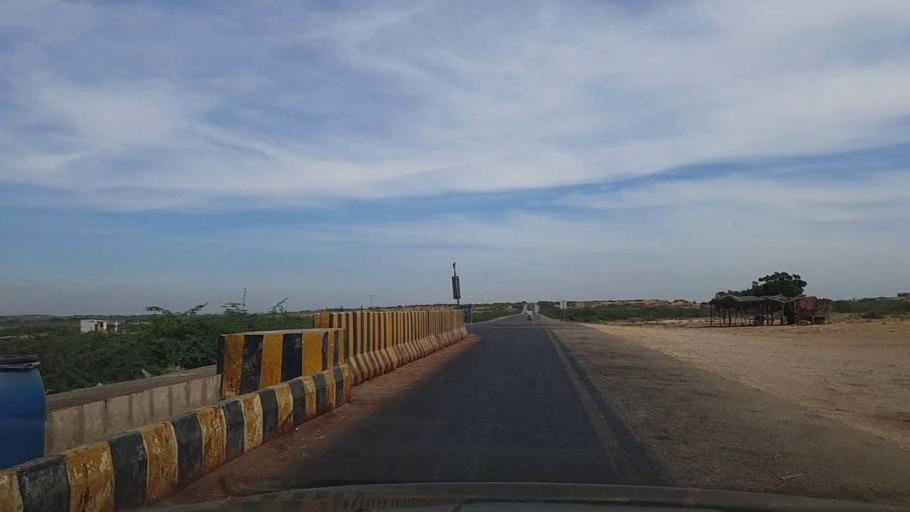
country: PK
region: Sindh
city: Thatta
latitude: 24.8453
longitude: 68.0102
